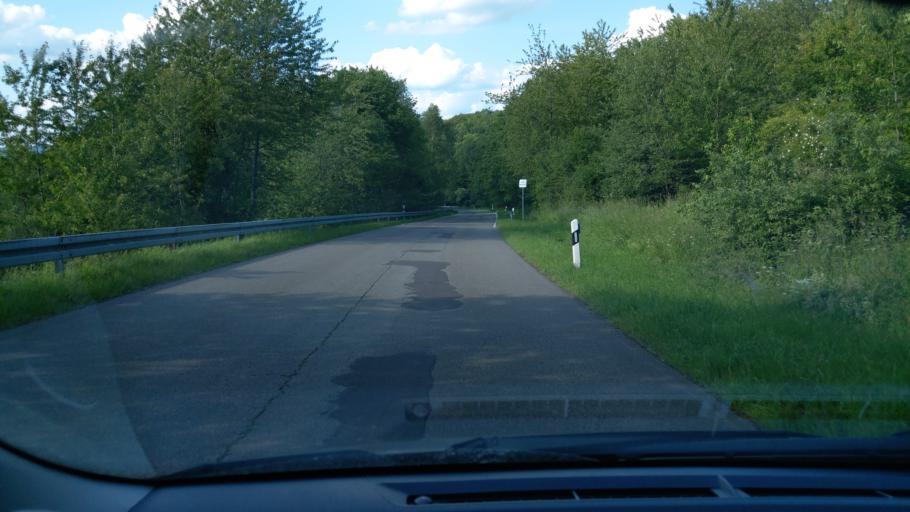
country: DE
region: Saarland
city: Wadern
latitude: 49.5041
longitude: 6.9257
